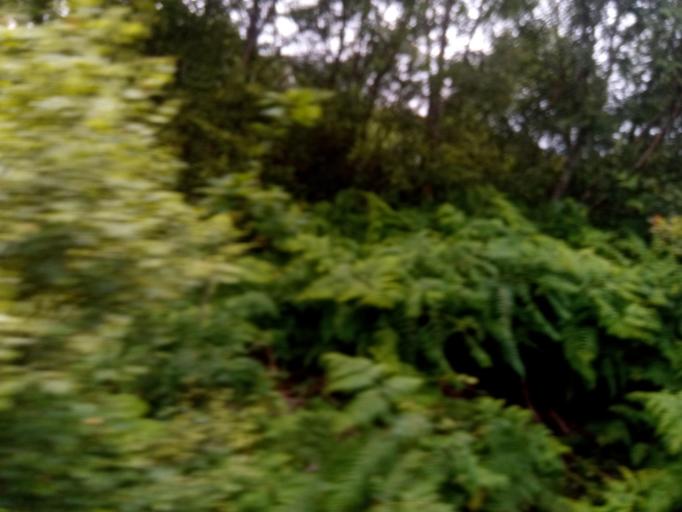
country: GB
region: Scotland
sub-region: Argyll and Bute
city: Isle Of Mull
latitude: 56.9639
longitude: -5.8156
